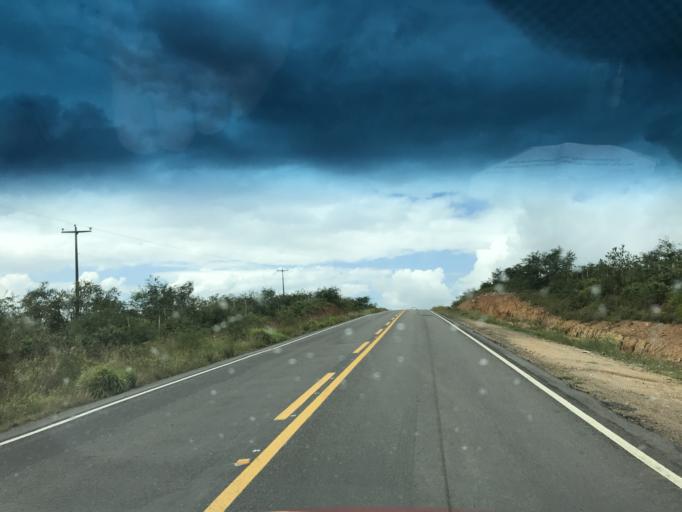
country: BR
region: Bahia
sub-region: Conceicao Do Almeida
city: Conceicao do Almeida
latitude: -12.6752
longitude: -39.2654
